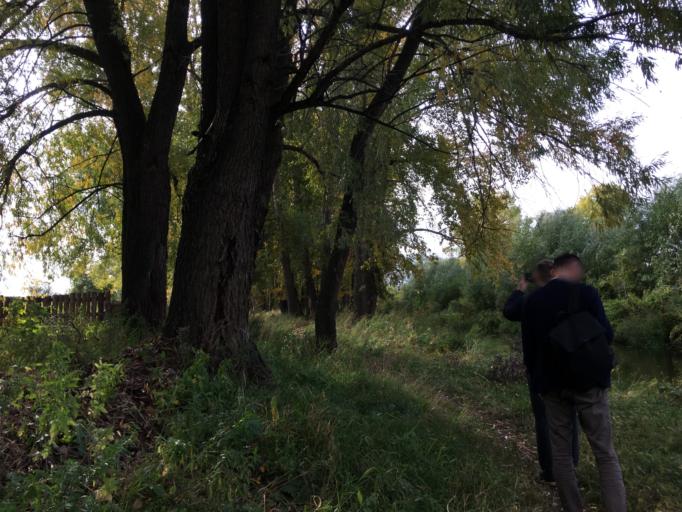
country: RU
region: Bashkortostan
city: Meleuz
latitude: 52.9587
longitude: 55.9212
